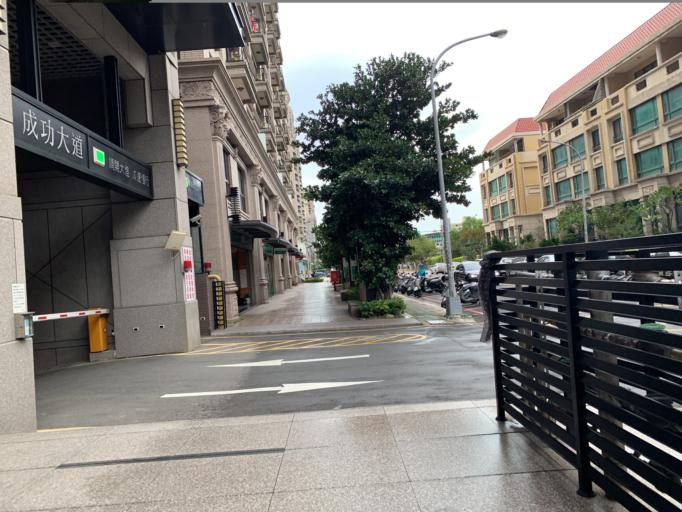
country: TW
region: Taiwan
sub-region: Hsinchu
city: Zhubei
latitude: 24.8174
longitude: 121.0187
